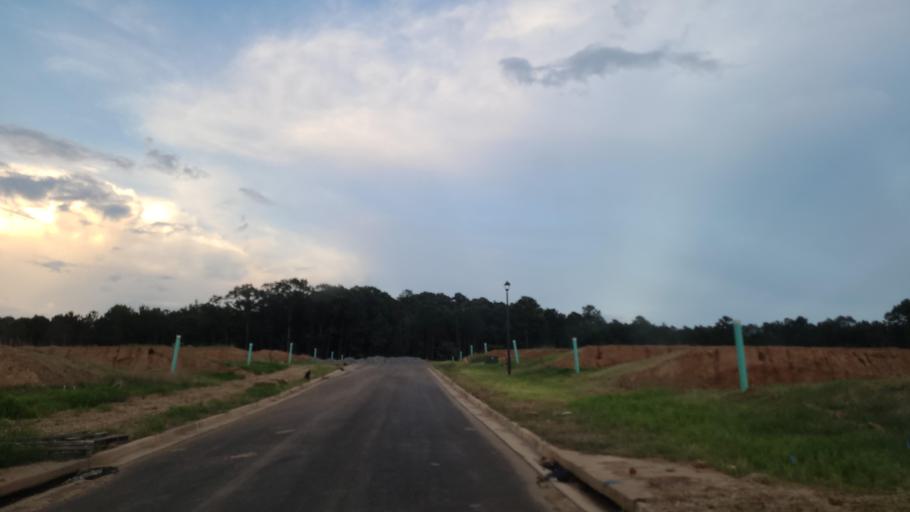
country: US
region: Georgia
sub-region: Bartow County
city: Cartersville
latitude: 34.2127
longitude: -84.7862
